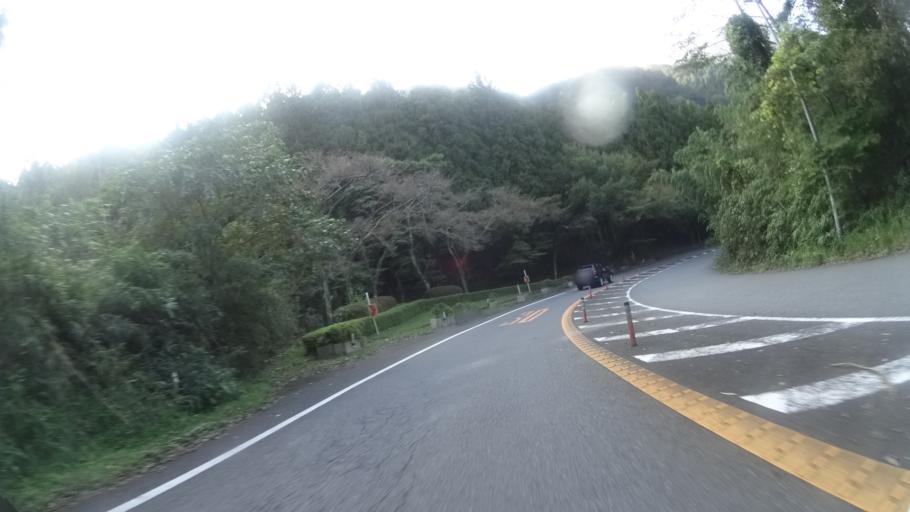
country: JP
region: Oita
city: Beppu
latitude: 33.2716
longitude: 131.4440
